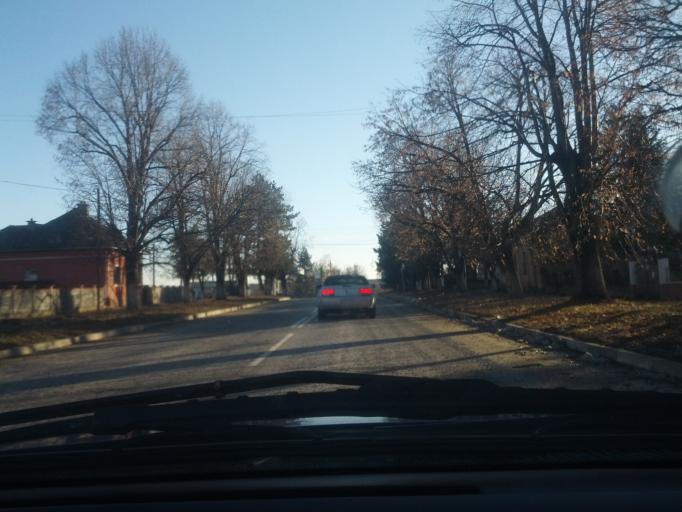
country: BG
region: Vratsa
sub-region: Obshtina Miziya
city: Miziya
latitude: 43.5932
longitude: 23.8187
